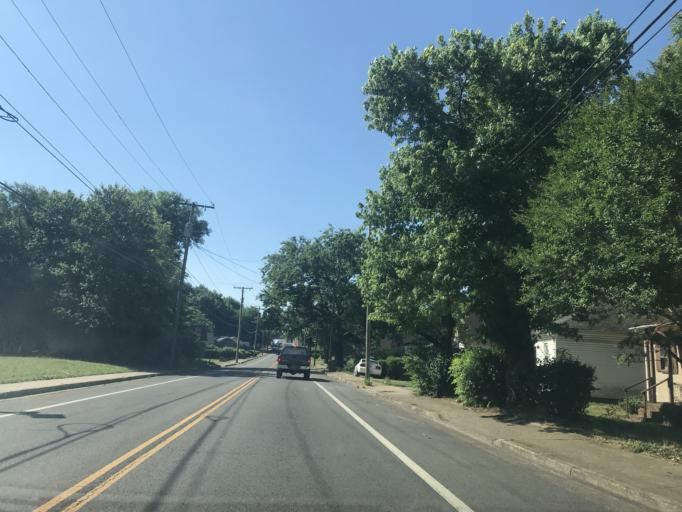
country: US
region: Tennessee
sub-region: Davidson County
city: Nashville
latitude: 36.1791
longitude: -86.8107
